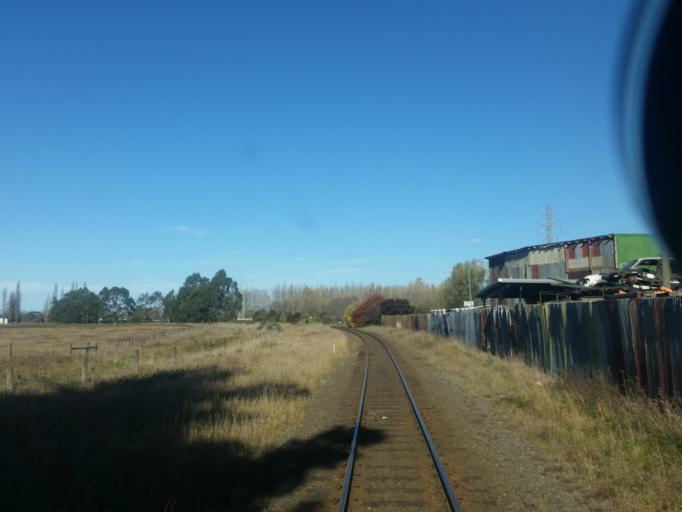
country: NZ
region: Canterbury
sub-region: Waimakariri District
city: Kaiapoi
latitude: -43.3280
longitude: 172.6023
